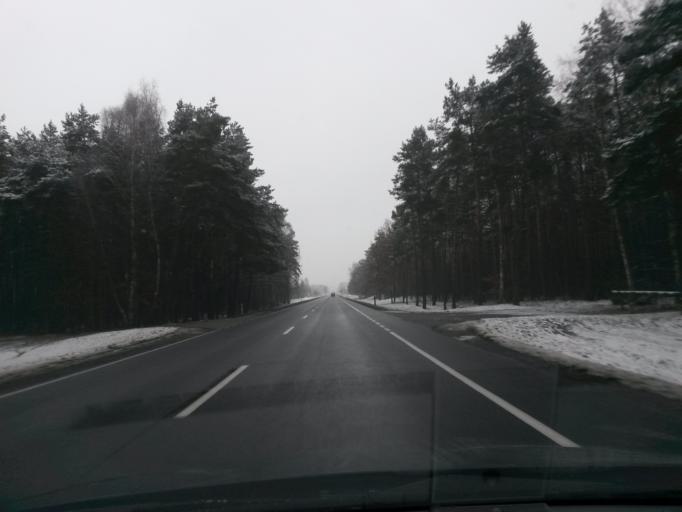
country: PL
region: Kujawsko-Pomorskie
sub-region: Powiat bydgoski
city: Biale Blota
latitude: 53.1181
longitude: 17.8828
